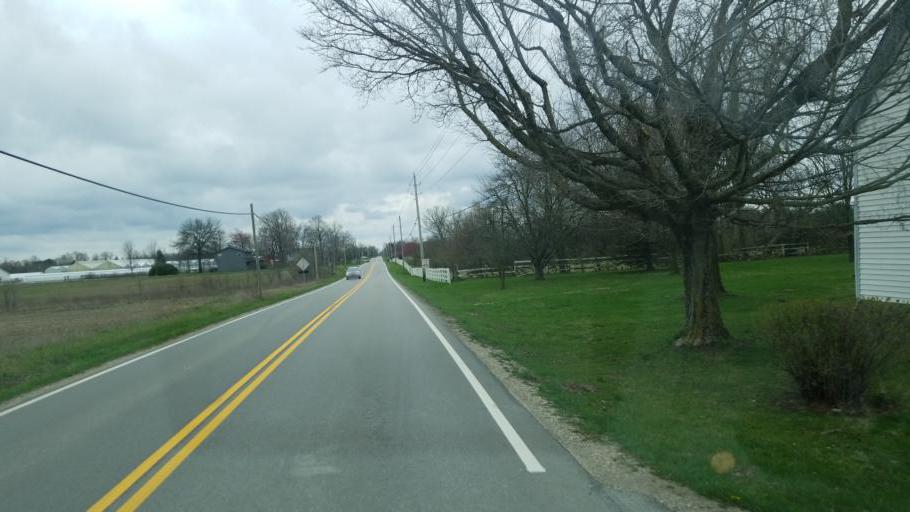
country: US
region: Ohio
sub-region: Delaware County
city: Delaware
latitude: 40.2368
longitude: -83.1316
